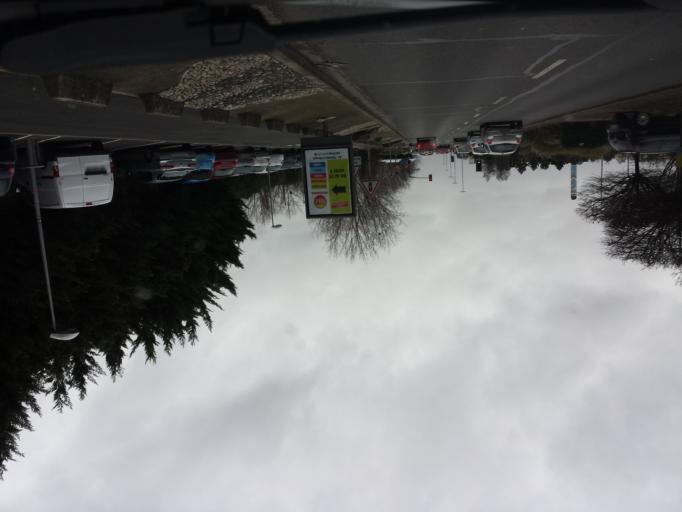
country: FR
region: Ile-de-France
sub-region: Departement du Val-d'Oise
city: Franconville
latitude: 48.9831
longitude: 2.2440
